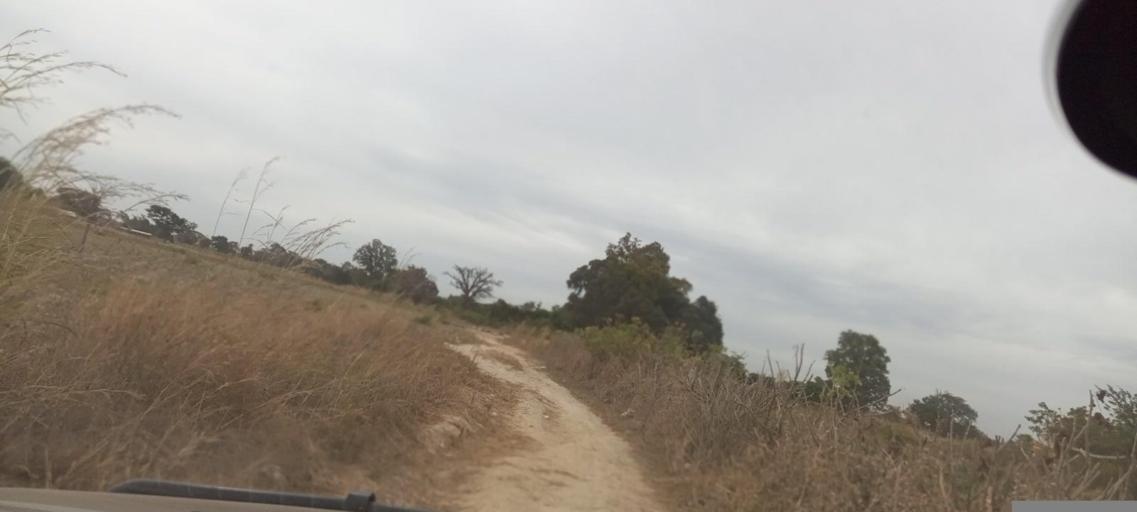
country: ML
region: Koulikoro
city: Kati
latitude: 12.7530
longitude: -8.3120
